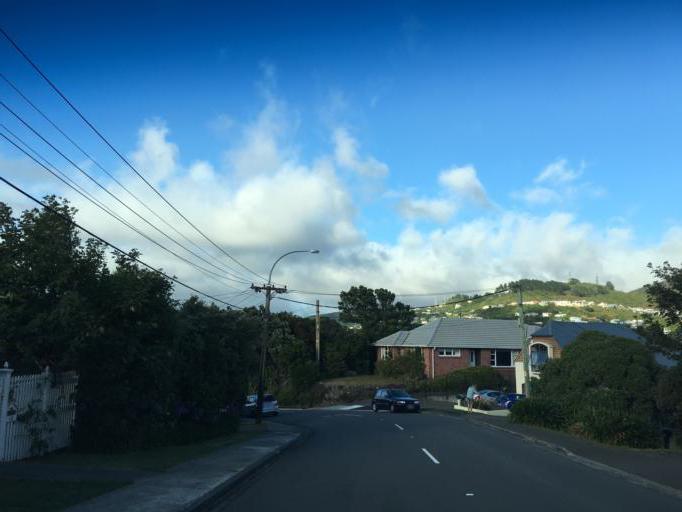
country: NZ
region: Wellington
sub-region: Wellington City
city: Kelburn
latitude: -41.2546
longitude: 174.7736
